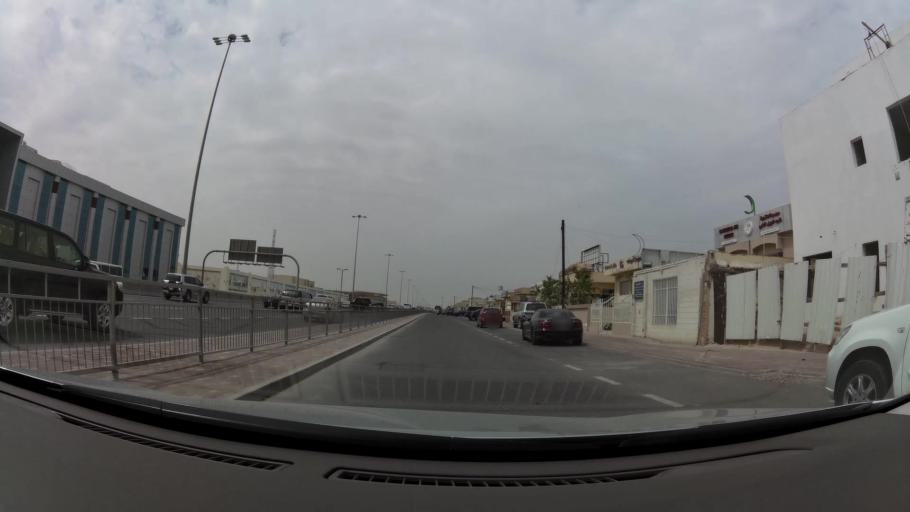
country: QA
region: Baladiyat ar Rayyan
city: Ar Rayyan
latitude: 25.3277
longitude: 51.4666
